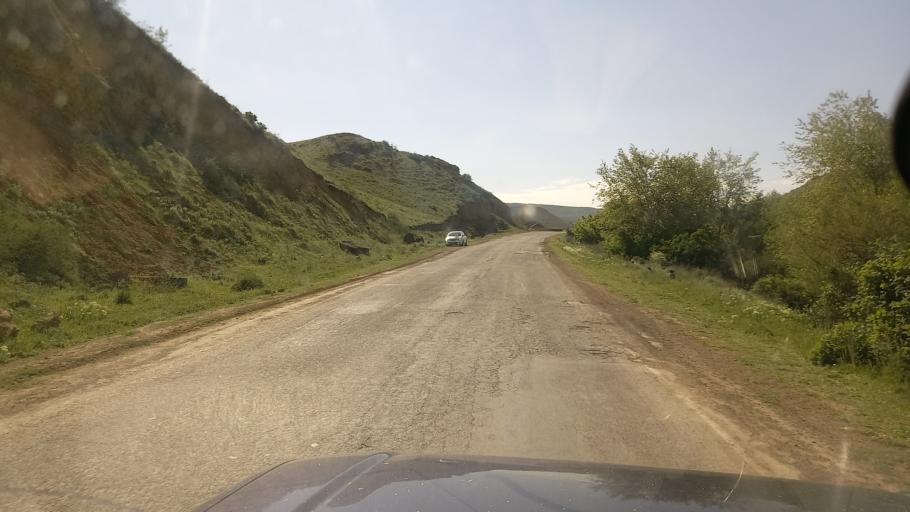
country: RU
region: Dagestan
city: Syrtych
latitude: 41.9399
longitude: 48.1812
